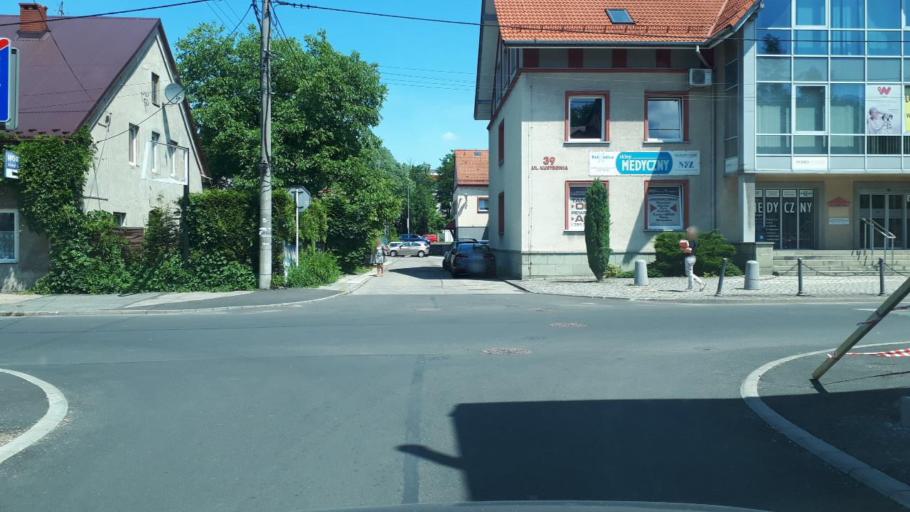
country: PL
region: Silesian Voivodeship
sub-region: Bielsko-Biala
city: Bielsko-Biala
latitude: 49.8014
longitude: 19.0473
